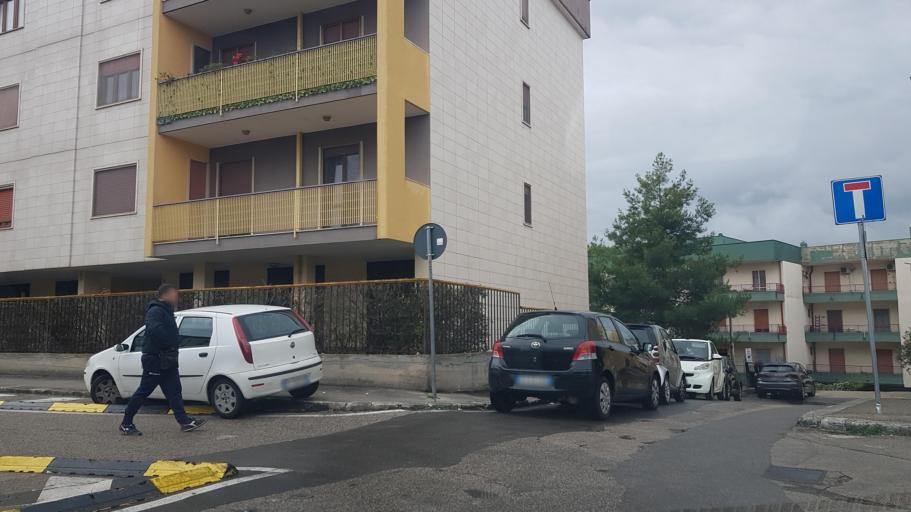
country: IT
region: Basilicate
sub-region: Provincia di Matera
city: Matera
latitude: 40.6784
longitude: 16.5868
